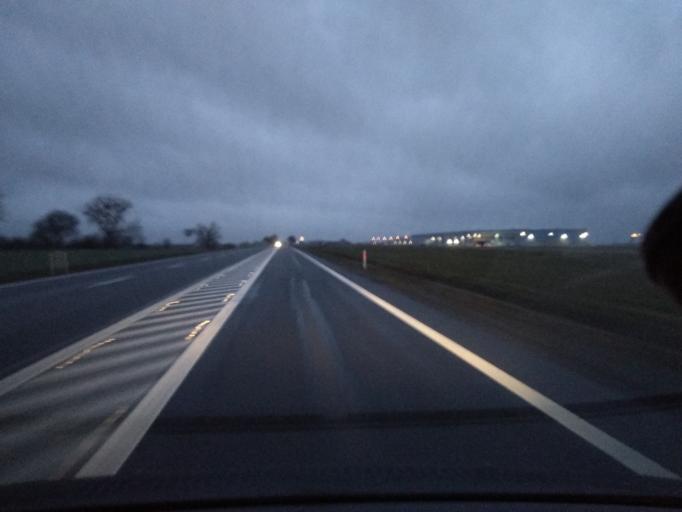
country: PL
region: Lower Silesian Voivodeship
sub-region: Powiat sredzki
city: Szczepanow
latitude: 51.1637
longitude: 16.6597
